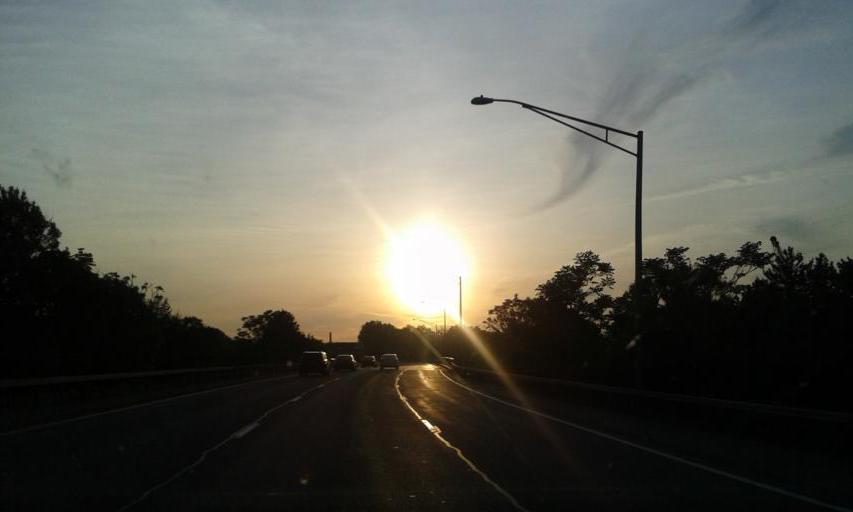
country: US
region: New York
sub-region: Onondaga County
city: Syracuse
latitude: 43.0562
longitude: -76.1745
